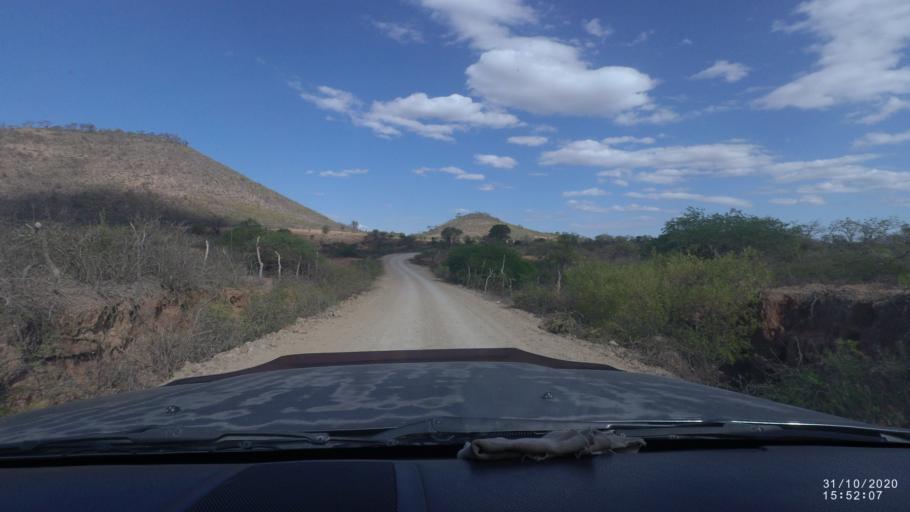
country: BO
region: Chuquisaca
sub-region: Provincia Zudanez
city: Mojocoya
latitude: -18.3177
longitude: -64.6963
